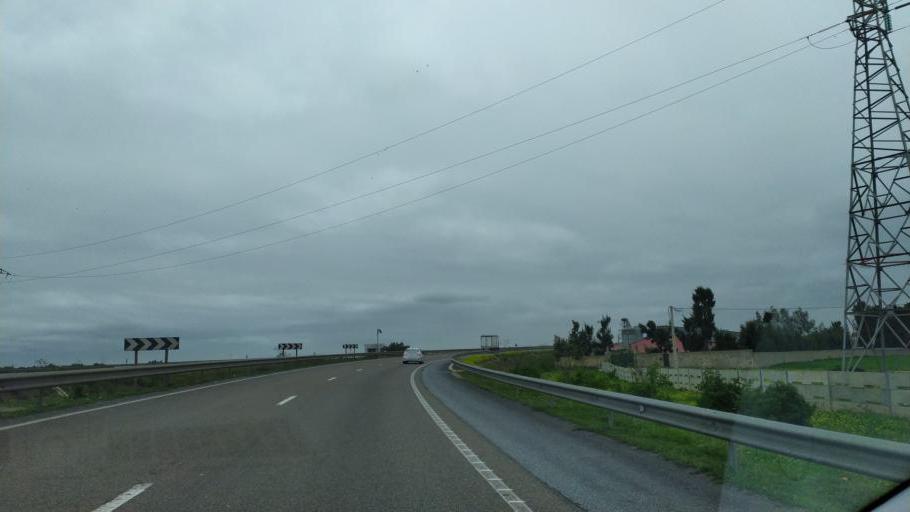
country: MA
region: Rabat-Sale-Zemmour-Zaer
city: Skhirat
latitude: 33.8750
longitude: -7.0086
